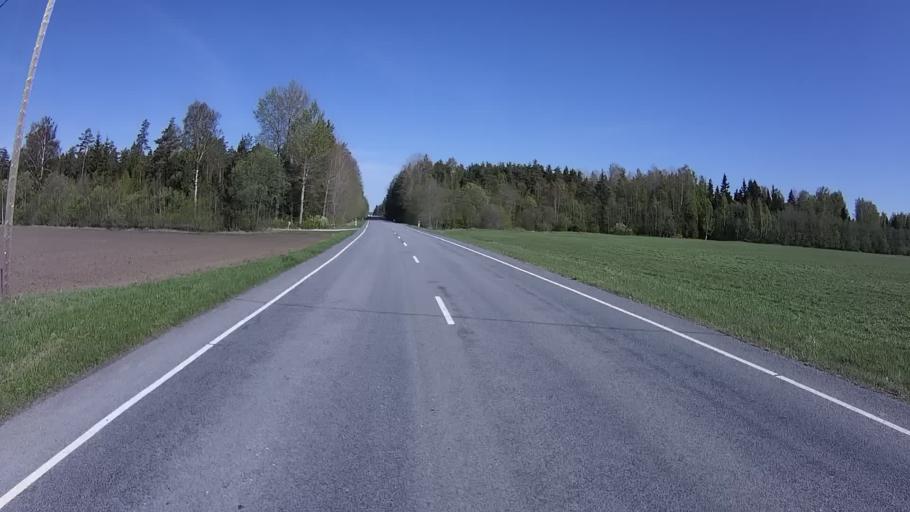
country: EE
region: Raplamaa
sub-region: Jaervakandi vald
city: Jarvakandi
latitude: 58.8491
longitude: 24.7953
